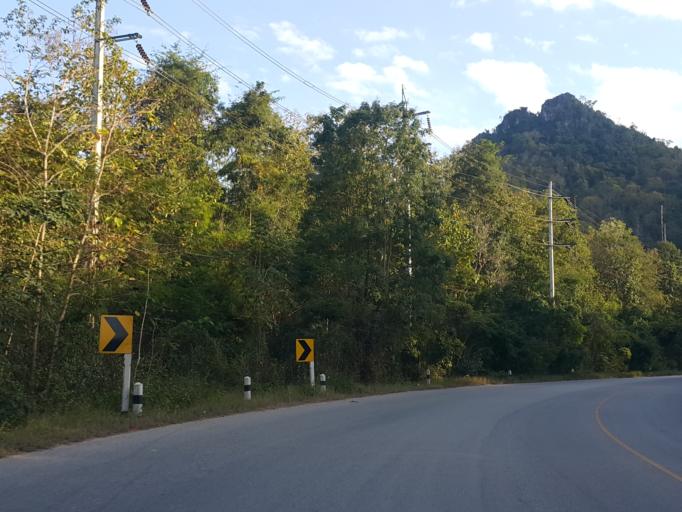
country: TH
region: Lampang
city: Chae Hom
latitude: 18.5105
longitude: 99.5549
